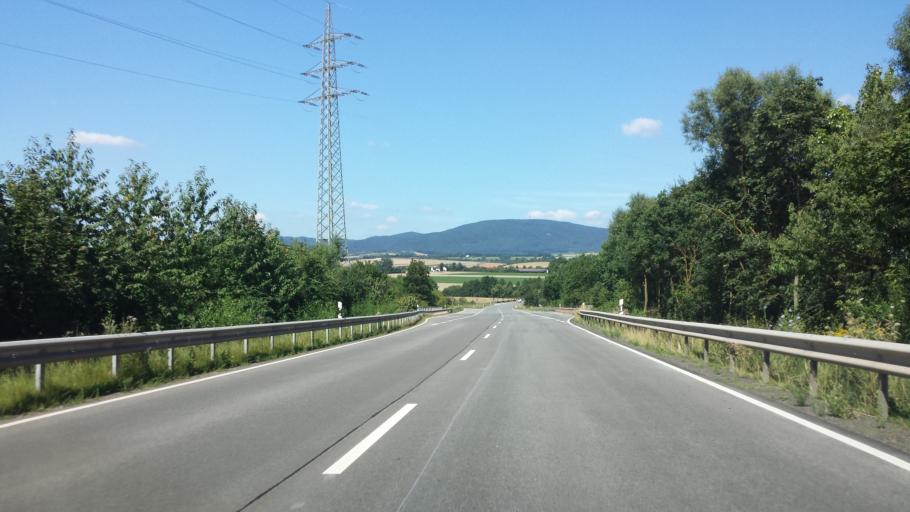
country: DE
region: Rheinland-Pfalz
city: Gollheim
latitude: 49.5945
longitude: 8.0315
